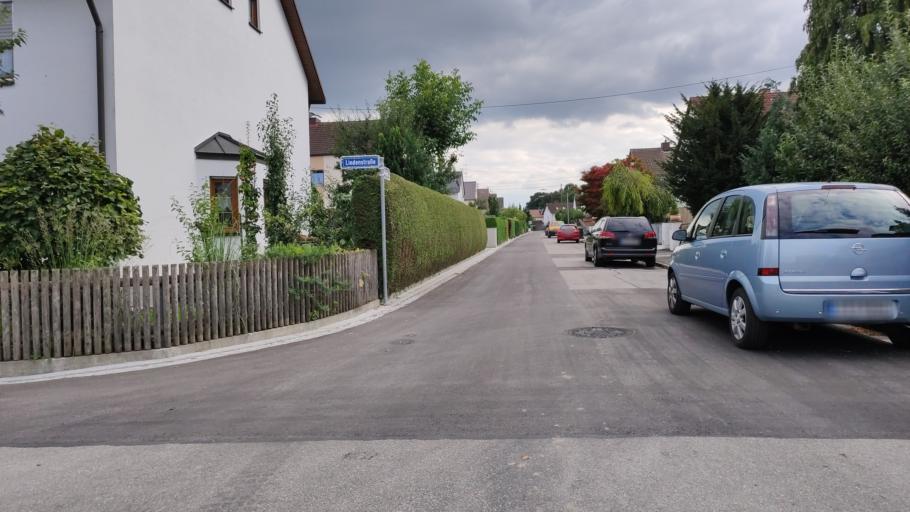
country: DE
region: Bavaria
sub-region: Swabia
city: Konigsbrunn
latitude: 48.2590
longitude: 10.8958
